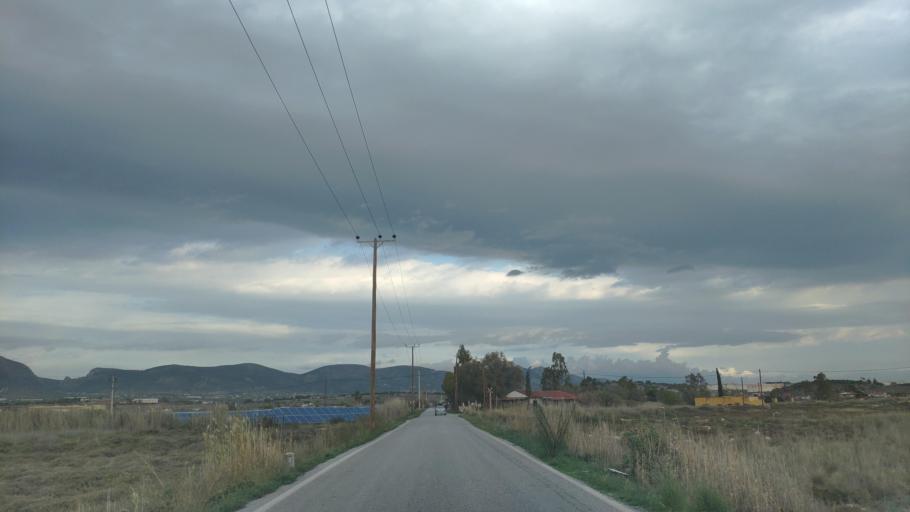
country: GR
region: Attica
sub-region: Nomarchia Dytikis Attikis
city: Nea Peramos
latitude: 37.9853
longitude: 23.3877
